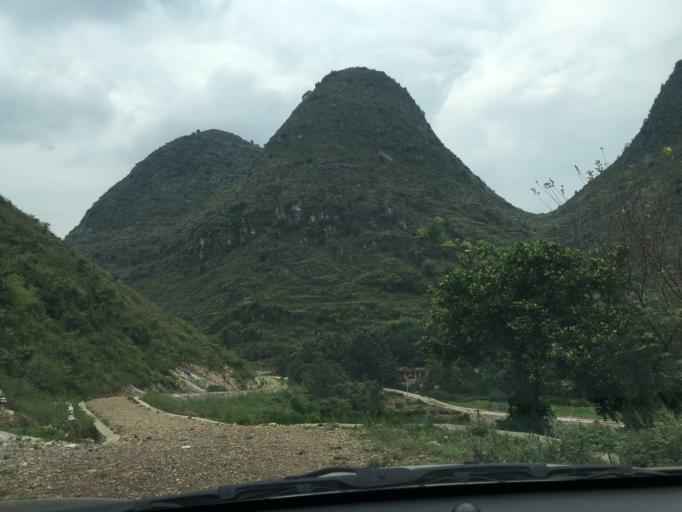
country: CN
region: Guangxi Zhuangzu Zizhiqu
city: Xinzhou
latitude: 25.3738
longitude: 105.6321
